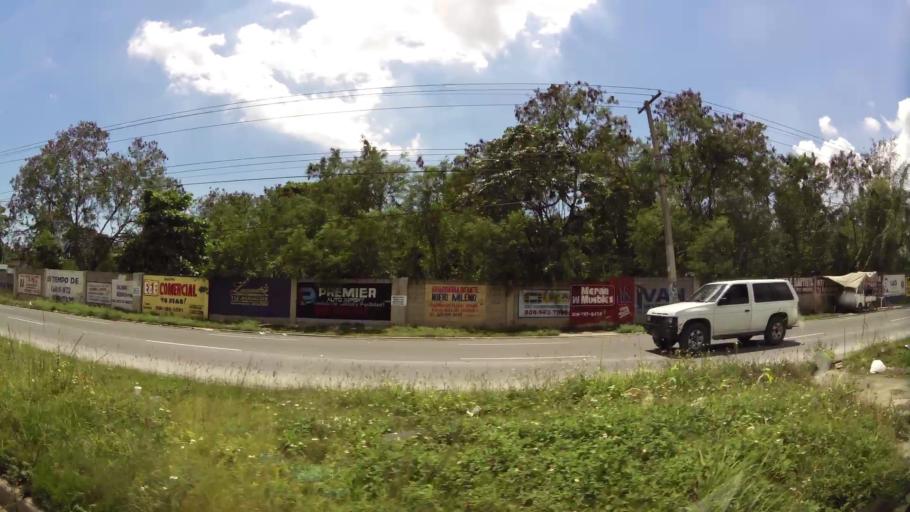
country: DO
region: Nacional
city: Ensanche Luperon
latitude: 18.5455
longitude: -69.8756
